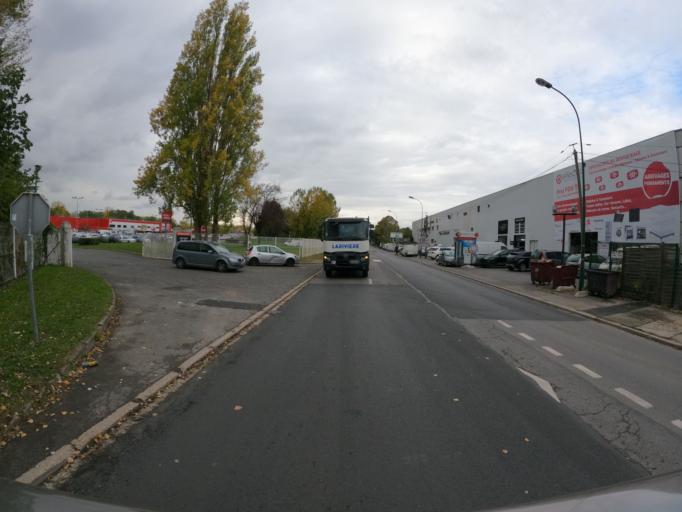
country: FR
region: Ile-de-France
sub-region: Departement de Seine-et-Marne
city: Brou-sur-Chantereine
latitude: 48.8692
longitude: 2.6227
